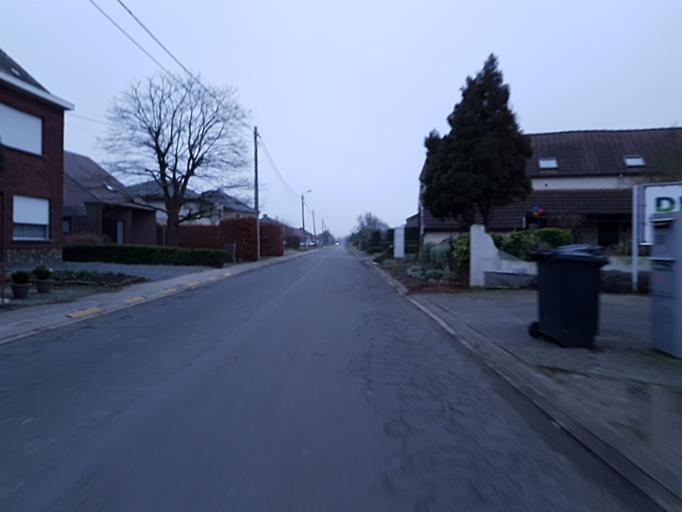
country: BE
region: Flanders
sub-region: Provincie Vlaams-Brabant
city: Boortmeerbeek
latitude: 50.9635
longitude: 4.5956
